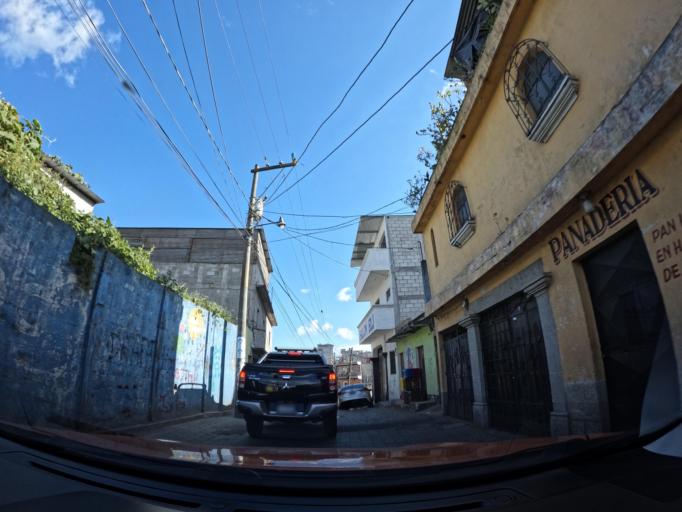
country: GT
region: Sacatepequez
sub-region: Municipio de Santa Maria de Jesus
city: Santa Maria de Jesus
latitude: 14.4967
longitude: -90.7100
